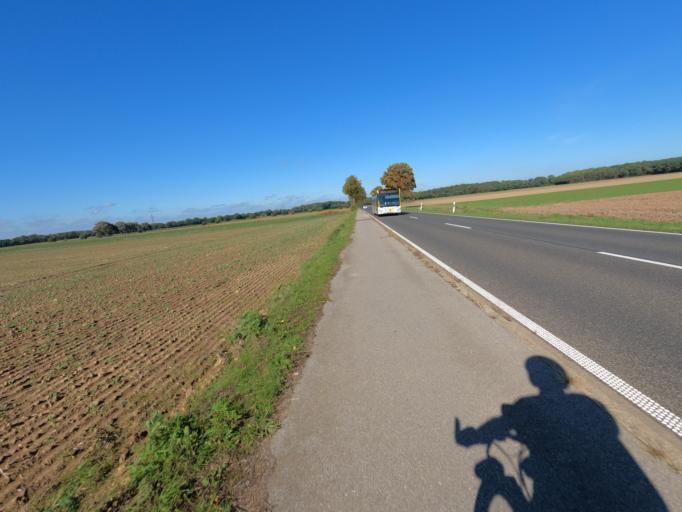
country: DE
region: North Rhine-Westphalia
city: Erkelenz
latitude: 51.0442
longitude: 6.3229
